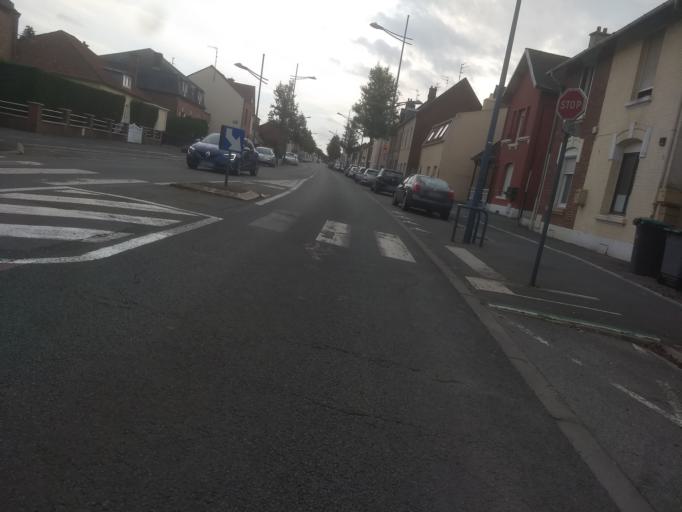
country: FR
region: Nord-Pas-de-Calais
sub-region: Departement du Pas-de-Calais
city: Beaurains
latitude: 50.2698
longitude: 2.7843
